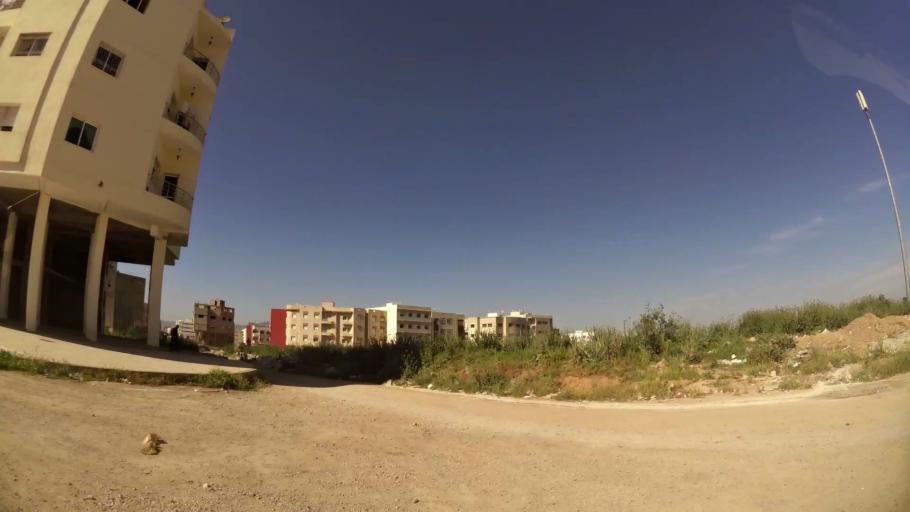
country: MA
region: Fes-Boulemane
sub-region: Fes
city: Fes
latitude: 34.0009
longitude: -5.0054
